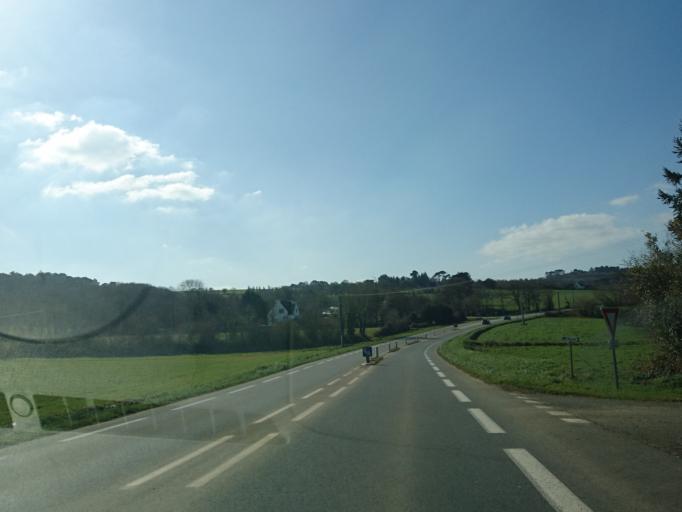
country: FR
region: Brittany
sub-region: Departement du Finistere
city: Hopital-Camfrout
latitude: 48.2812
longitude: -4.2317
